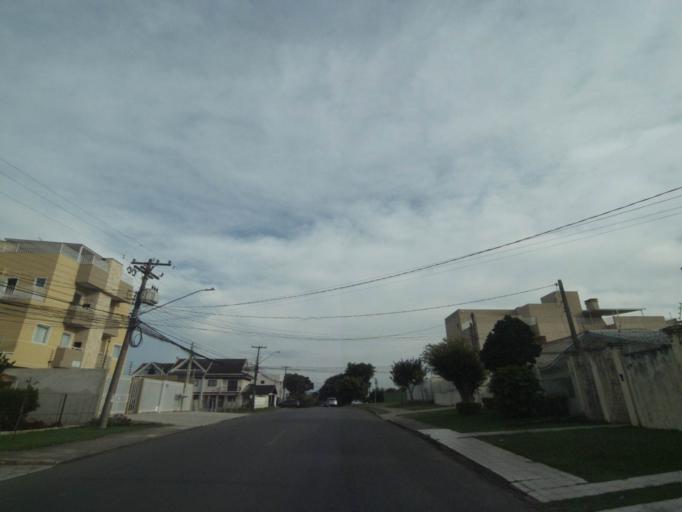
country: BR
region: Parana
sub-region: Pinhais
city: Pinhais
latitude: -25.4521
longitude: -49.2200
